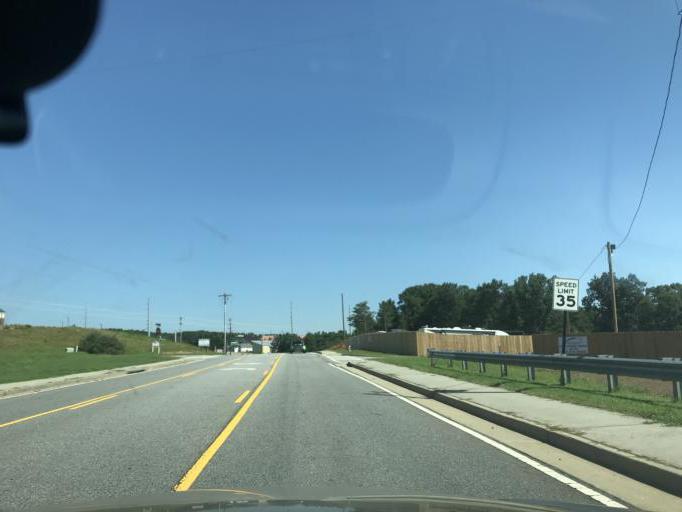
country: US
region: Georgia
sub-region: Forsyth County
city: Cumming
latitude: 34.1947
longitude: -84.1323
